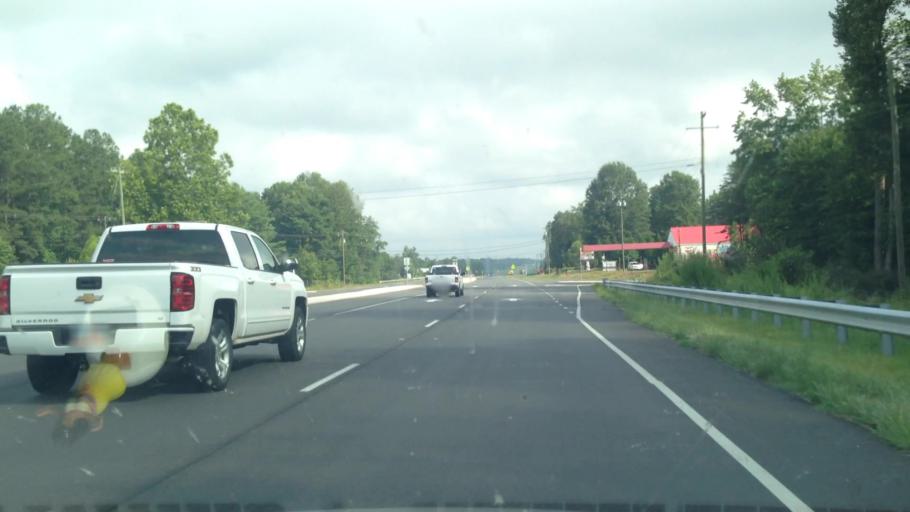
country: US
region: North Carolina
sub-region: Guilford County
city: Summerfield
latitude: 36.2139
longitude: -79.9069
